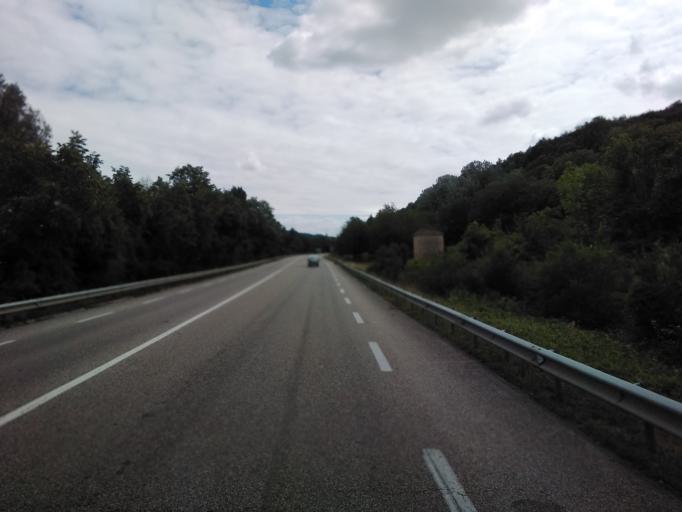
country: FR
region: Rhone-Alpes
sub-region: Departement de l'Ain
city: Lagnieu
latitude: 45.8983
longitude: 5.3377
